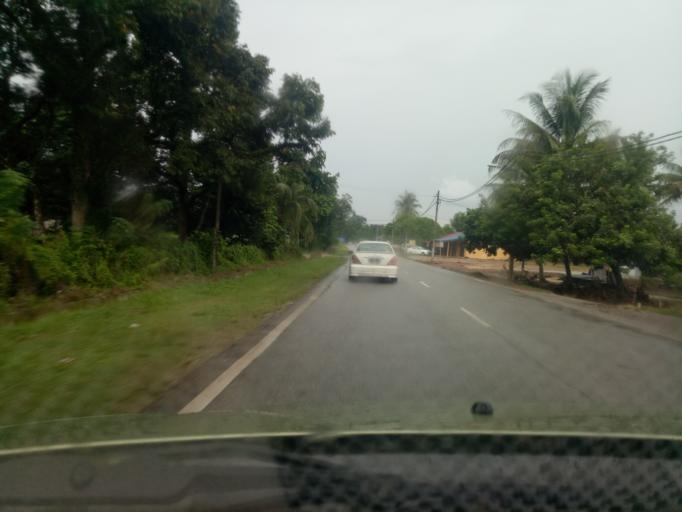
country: MY
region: Penang
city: Tasek Glugor
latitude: 5.5339
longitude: 100.5708
